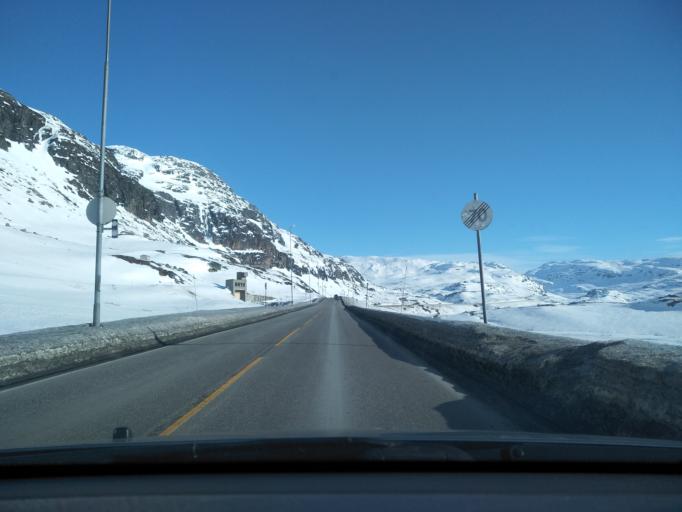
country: NO
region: Hordaland
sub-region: Odda
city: Odda
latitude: 59.8493
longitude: 6.9505
